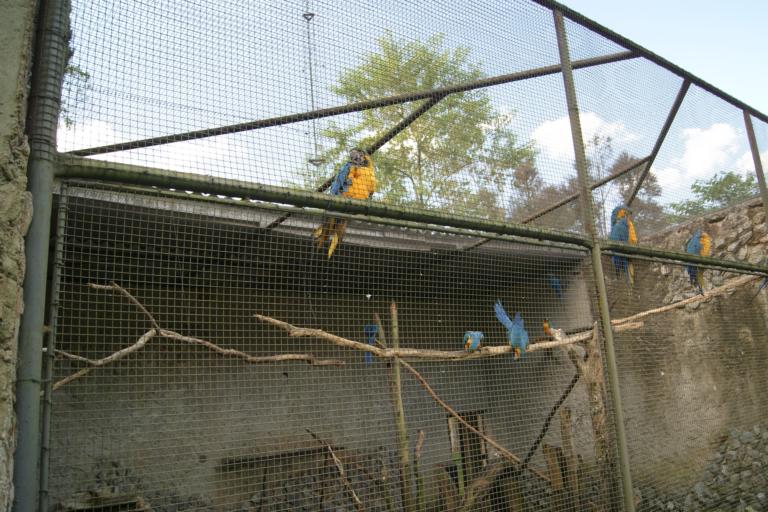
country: BR
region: Sao Paulo
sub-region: Sao Bernardo Do Campo
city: Sao Bernardo do Campo
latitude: -23.7734
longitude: -46.5145
